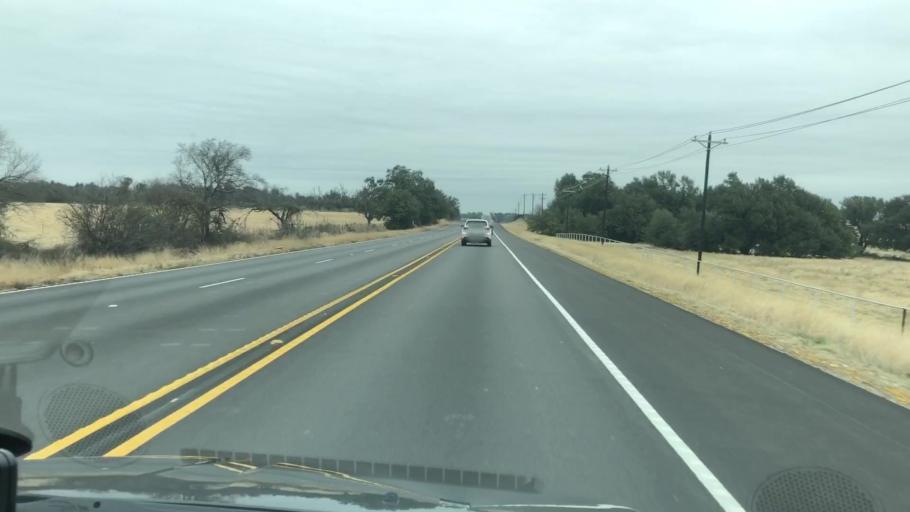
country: US
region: Texas
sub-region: Erath County
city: Stephenville
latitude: 32.3066
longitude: -98.1858
